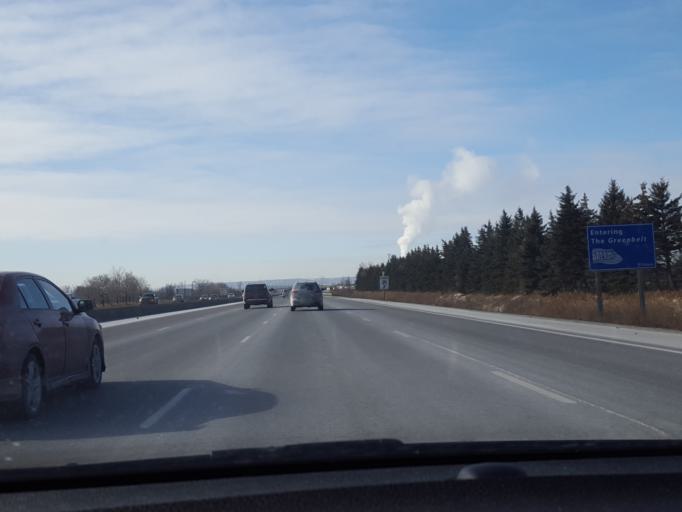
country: CA
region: Ontario
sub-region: Halton
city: Milton
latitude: 43.5795
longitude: -79.8203
